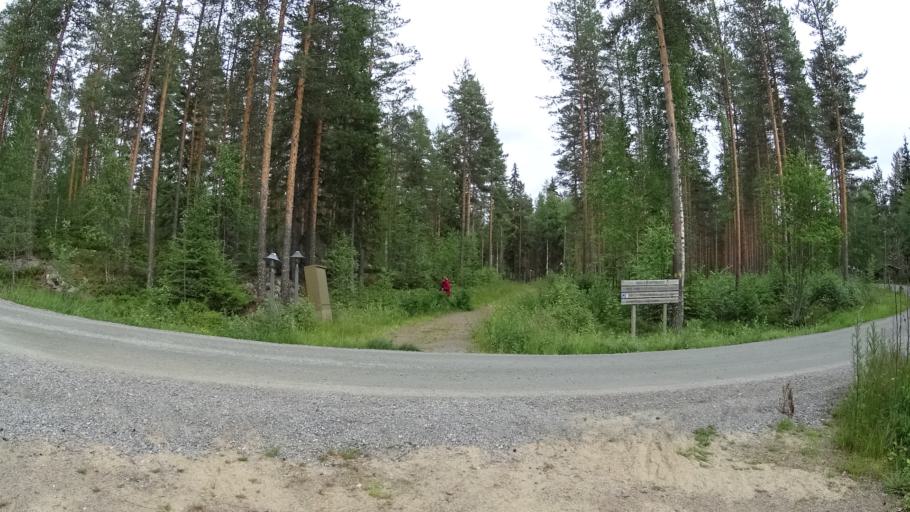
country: FI
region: Southern Ostrobothnia
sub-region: Kuusiokunnat
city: AEhtaeri
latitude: 62.5309
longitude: 24.1900
